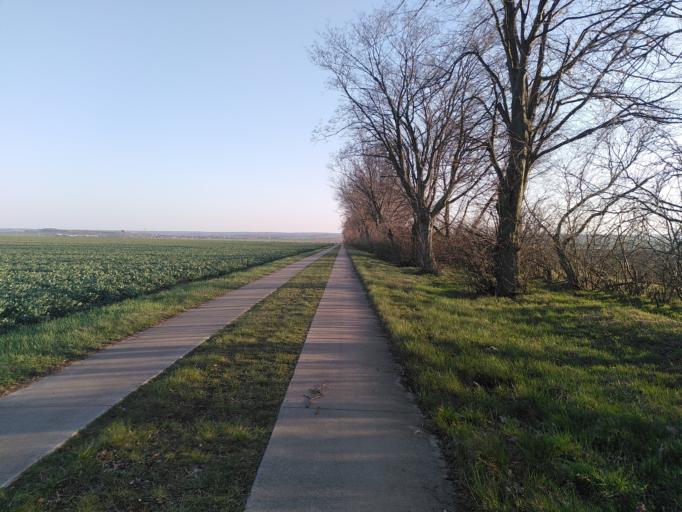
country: DE
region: Saxony-Anhalt
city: Ditfurt
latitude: 51.7988
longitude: 11.2301
